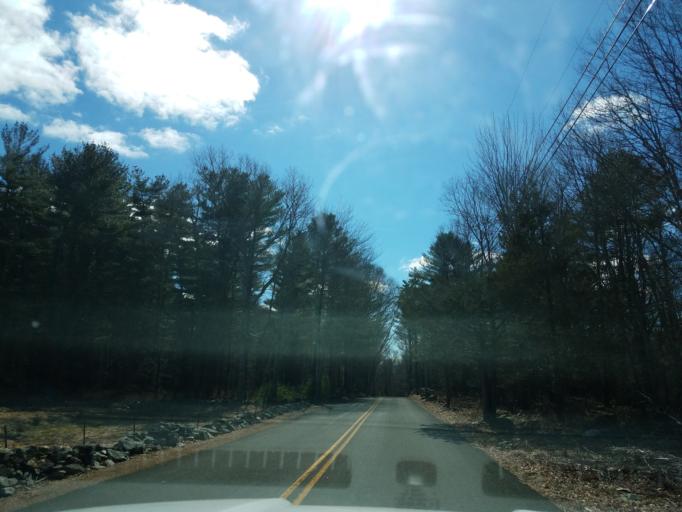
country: US
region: Connecticut
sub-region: Windham County
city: North Grosvenor Dale
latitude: 41.9864
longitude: -71.8886
